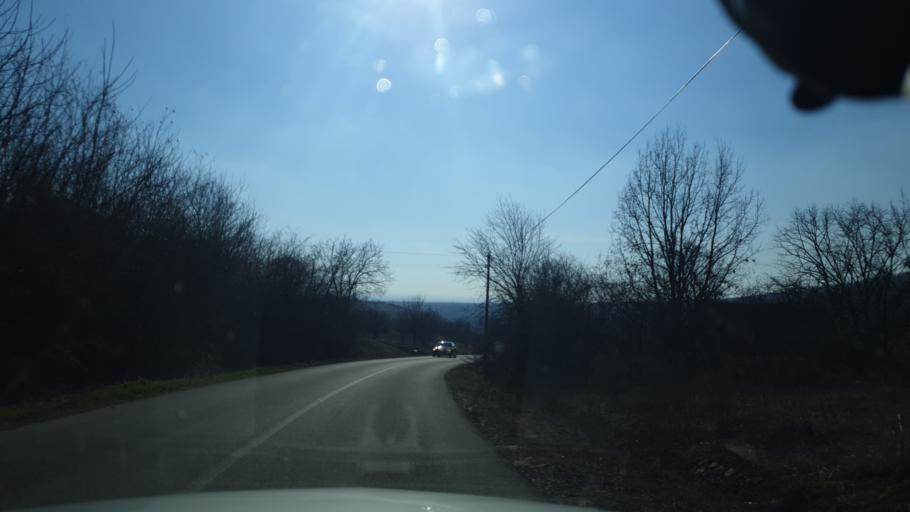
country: RS
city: Vrdnik
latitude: 45.1157
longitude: 19.7742
